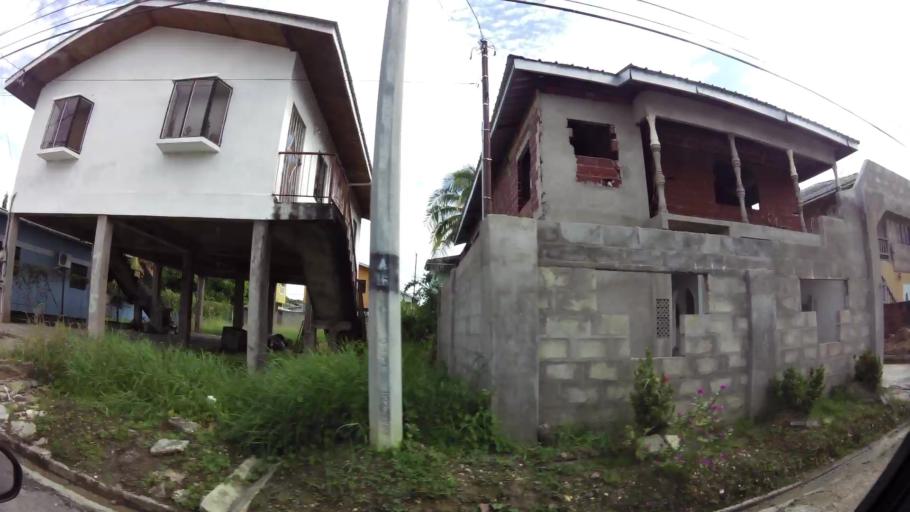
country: TT
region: Chaguanas
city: Chaguanas
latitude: 10.5100
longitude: -61.3941
